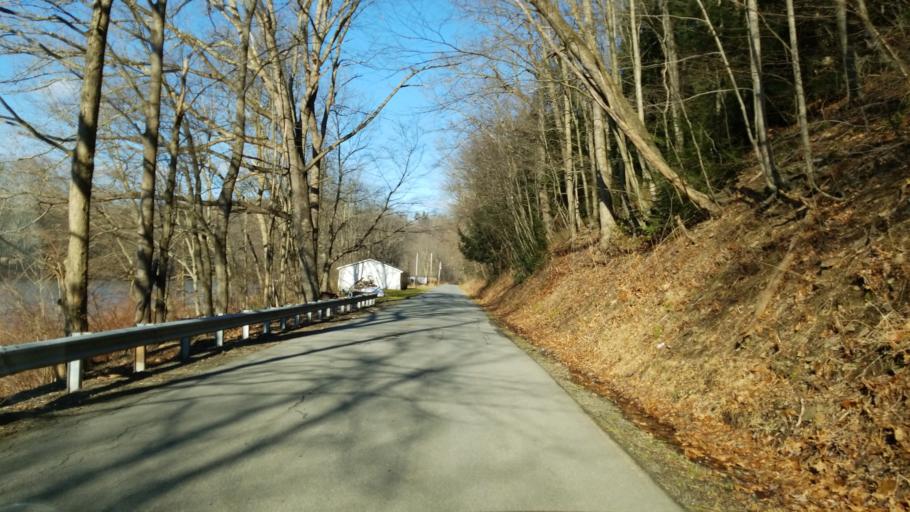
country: US
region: Pennsylvania
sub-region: Clearfield County
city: Curwensville
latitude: 40.9760
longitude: -78.4914
